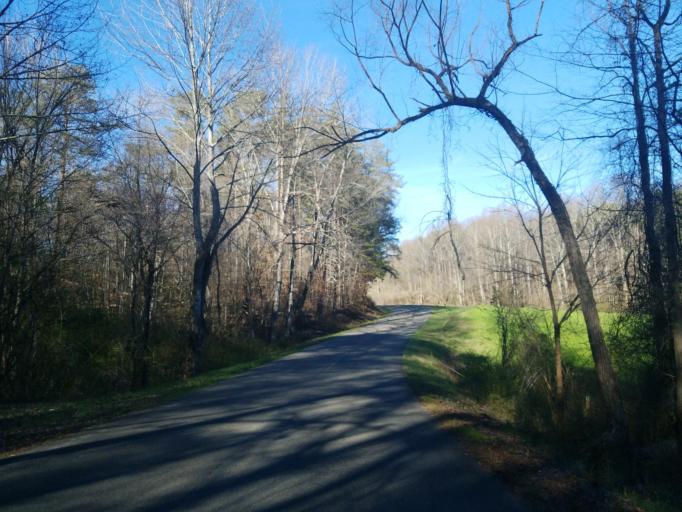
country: US
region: Georgia
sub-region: Gilmer County
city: Ellijay
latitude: 34.6448
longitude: -84.3462
